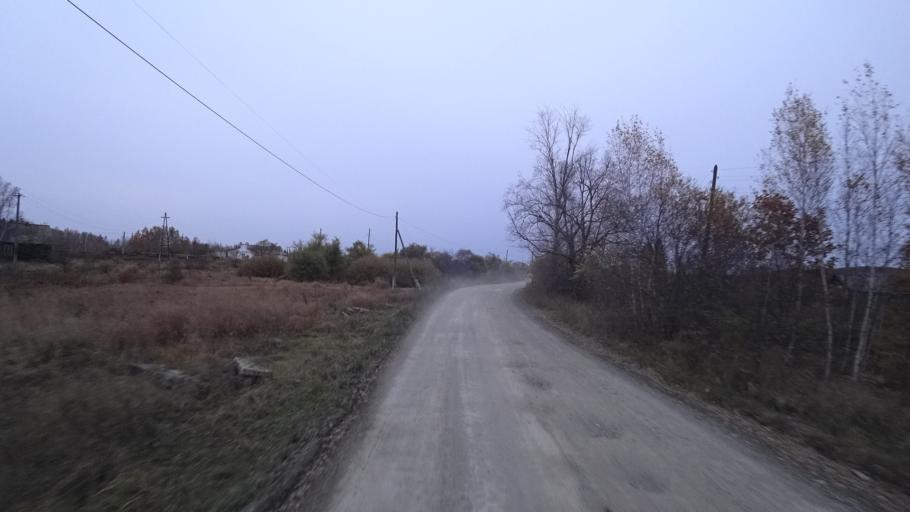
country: RU
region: Khabarovsk Krai
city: Amursk
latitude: 49.9023
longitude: 136.1430
